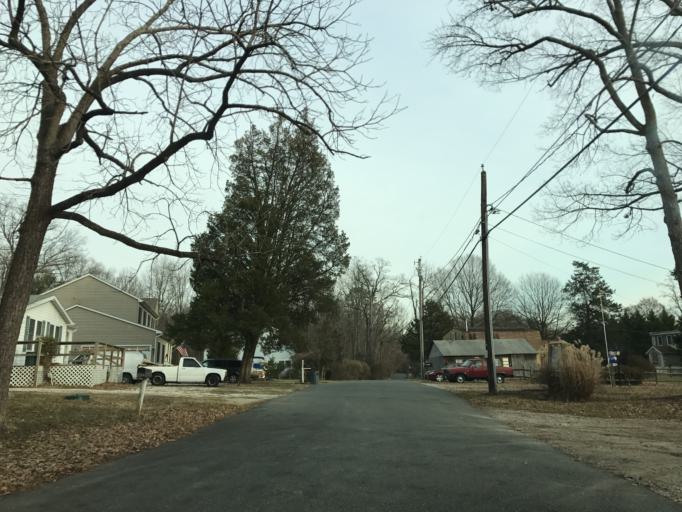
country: US
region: Maryland
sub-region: Baltimore County
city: White Marsh
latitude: 39.3863
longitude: -76.4099
